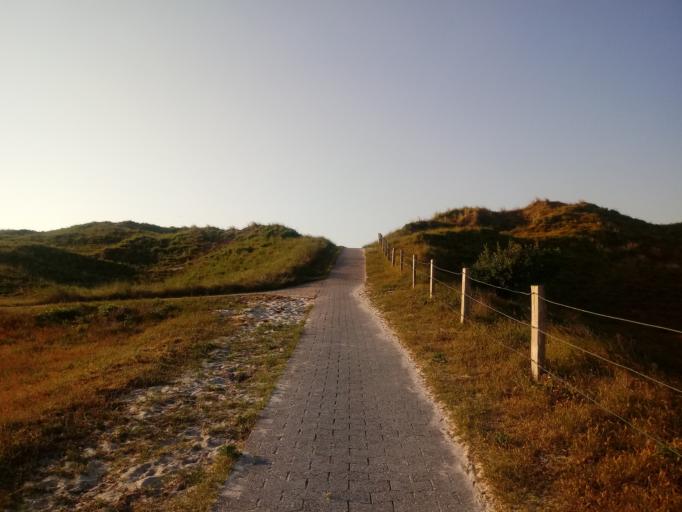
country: DE
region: Lower Saxony
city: Baltrum
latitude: 53.7328
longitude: 7.3968
